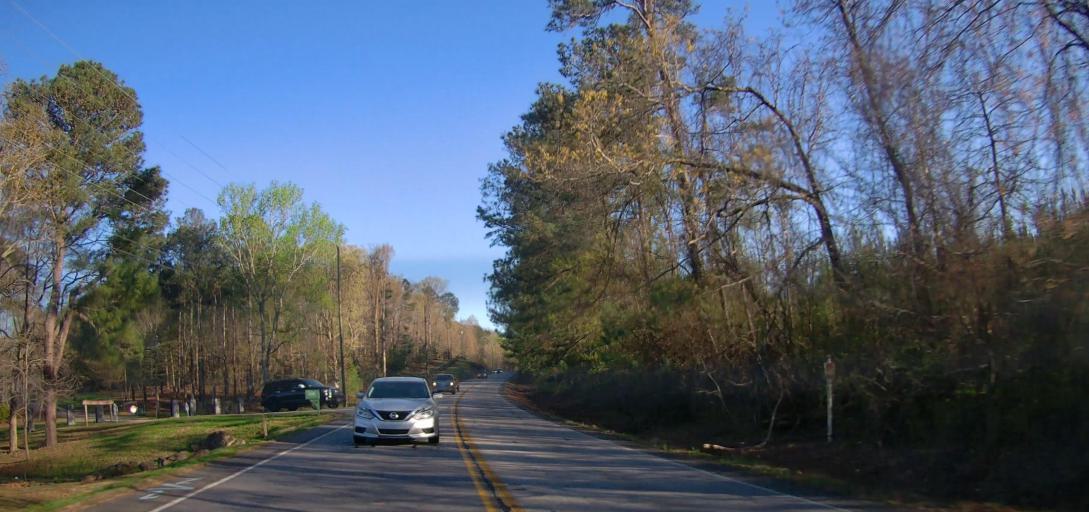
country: US
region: Georgia
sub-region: Newton County
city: Oakwood
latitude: 33.4370
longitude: -83.8978
